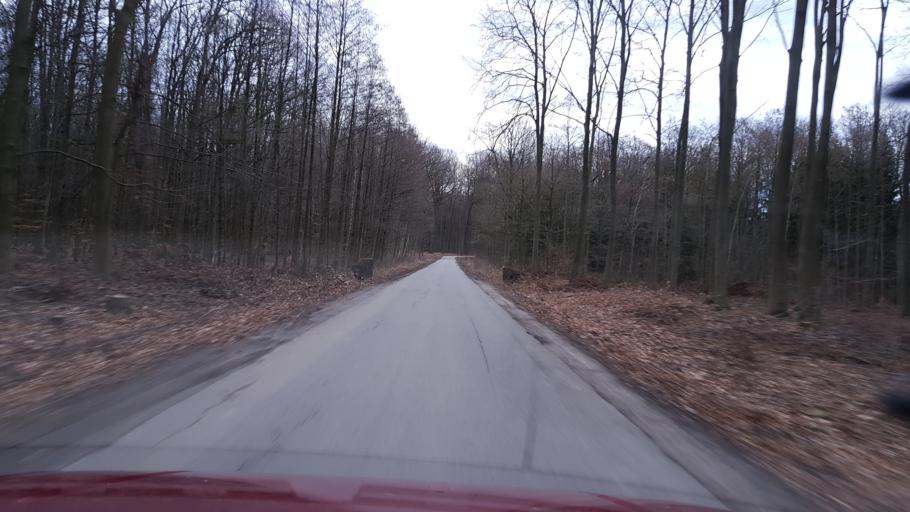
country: PL
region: West Pomeranian Voivodeship
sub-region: Powiat gryfinski
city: Stare Czarnowo
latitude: 53.3150
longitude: 14.7140
